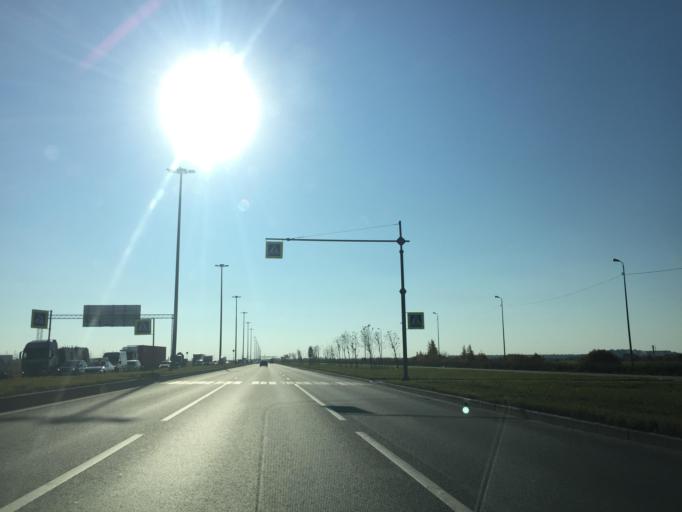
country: RU
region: St.-Petersburg
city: Petro-Slavyanka
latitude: 59.7788
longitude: 30.4978
